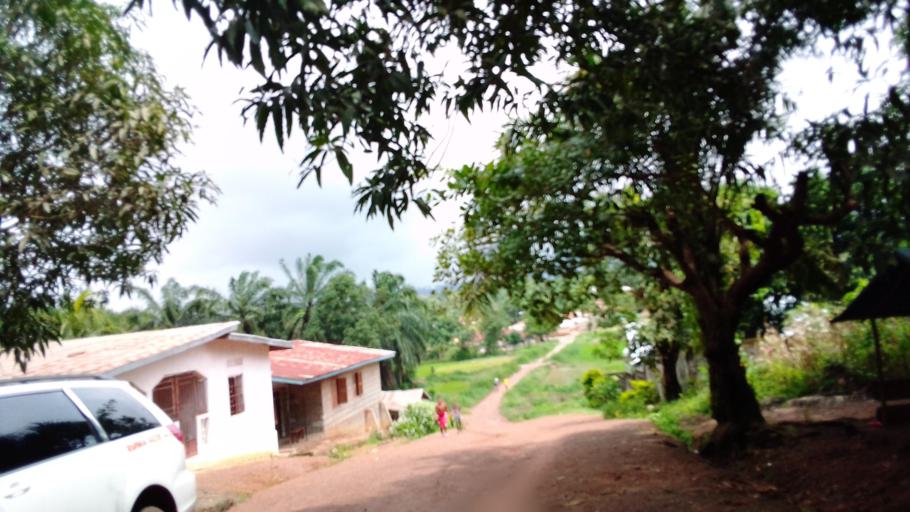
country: SL
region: Eastern Province
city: Kenema
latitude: 7.8636
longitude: -11.1747
